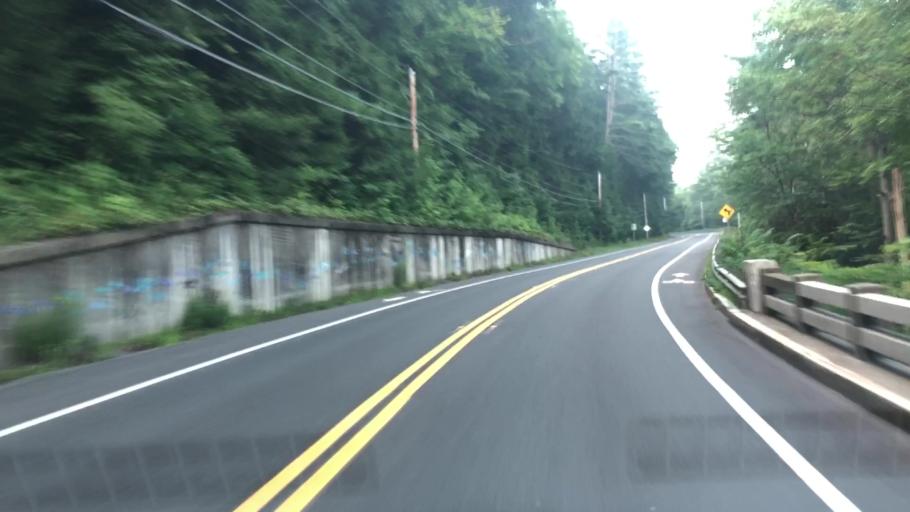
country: US
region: Massachusetts
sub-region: Franklin County
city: Buckland
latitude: 42.5592
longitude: -72.8041
